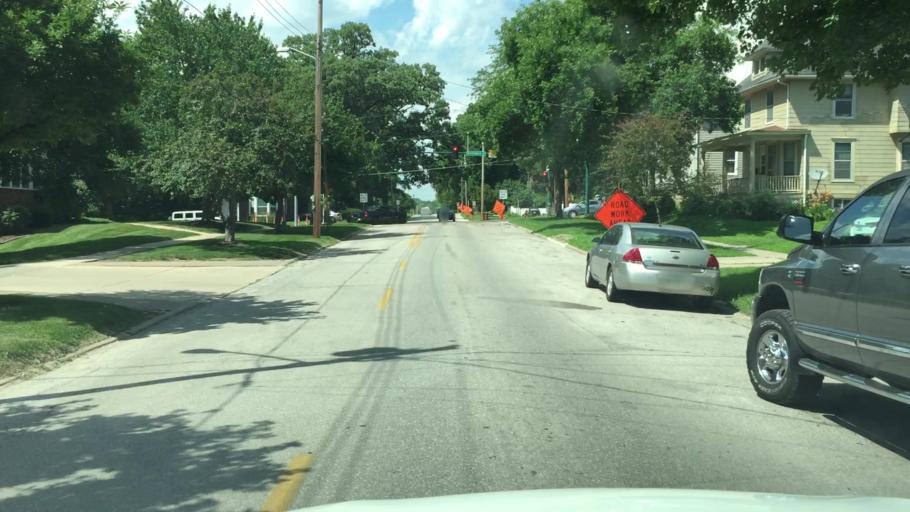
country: US
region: Iowa
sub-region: Johnson County
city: Iowa City
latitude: 41.6571
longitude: -91.5229
